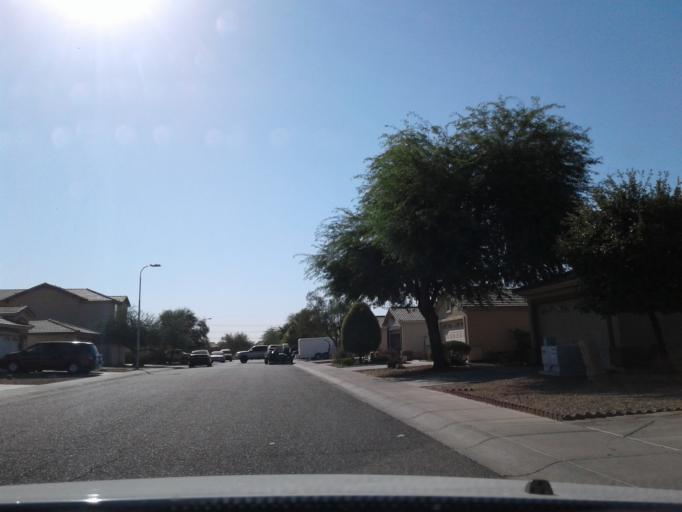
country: US
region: Arizona
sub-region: Maricopa County
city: Laveen
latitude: 33.4134
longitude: -112.1939
